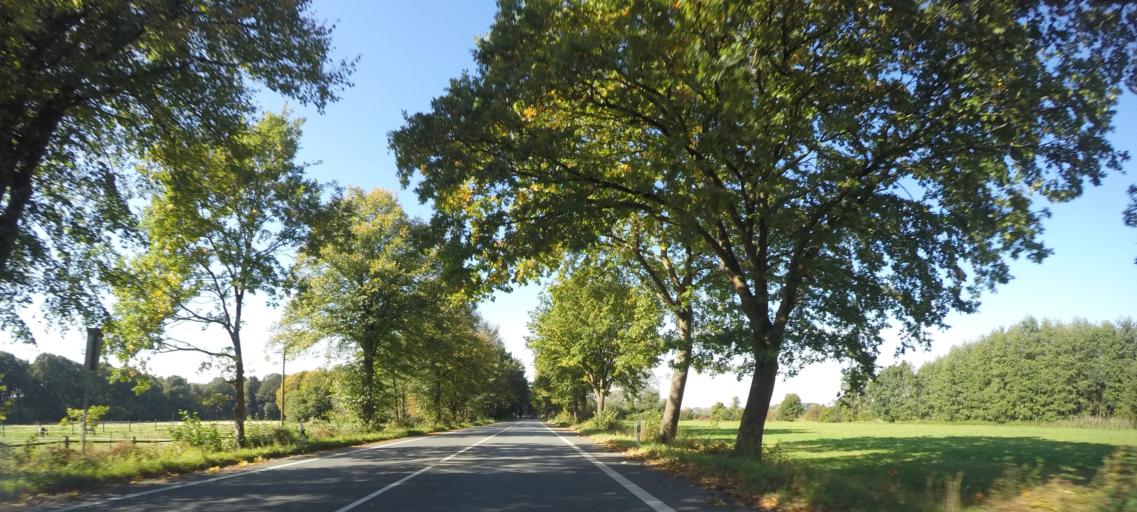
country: DE
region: North Rhine-Westphalia
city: Ahlen
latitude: 51.7002
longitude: 7.9100
